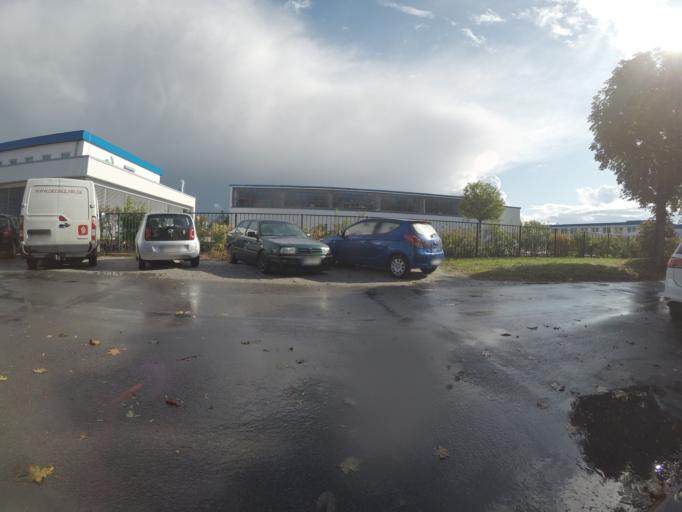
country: DE
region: Brandenburg
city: Strausberg
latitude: 52.5843
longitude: 13.8967
